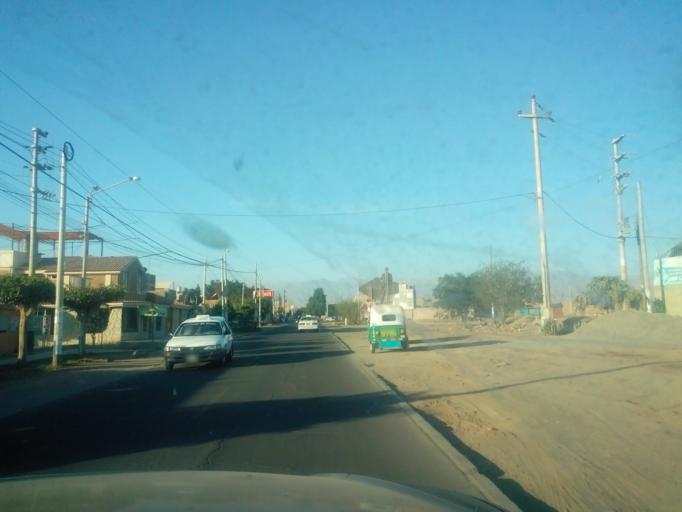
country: PE
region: Ica
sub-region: Provincia de Ica
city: Ica
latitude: -14.0806
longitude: -75.7486
